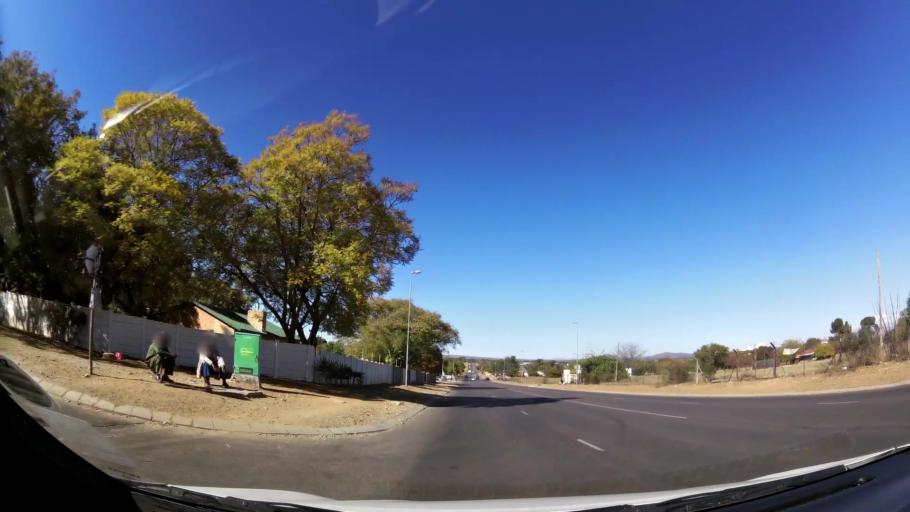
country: ZA
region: Limpopo
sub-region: Capricorn District Municipality
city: Polokwane
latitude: -23.9120
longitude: 29.4749
